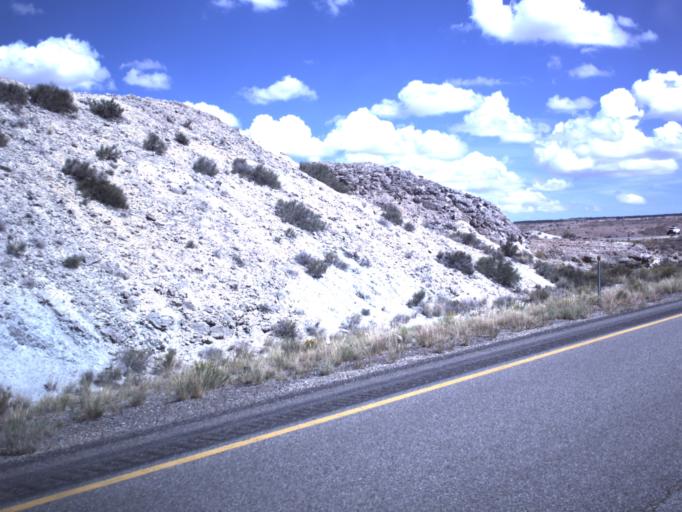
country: US
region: Utah
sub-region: Emery County
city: Ferron
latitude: 38.8450
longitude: -110.9886
